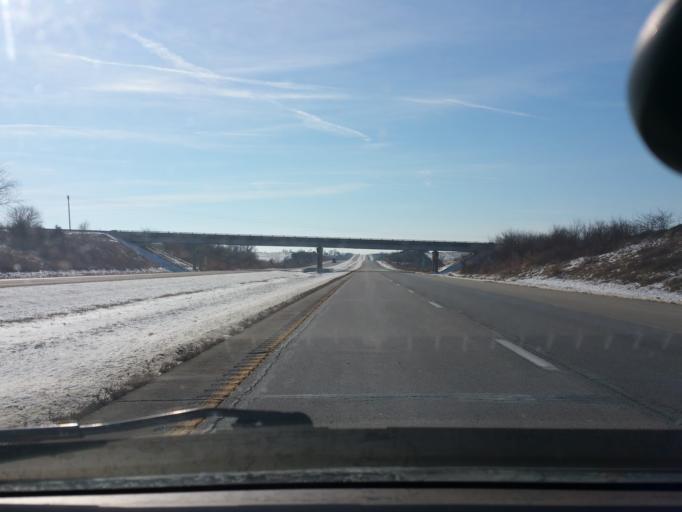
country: US
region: Iowa
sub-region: Decatur County
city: Lamoni
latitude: 40.5457
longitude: -93.9547
